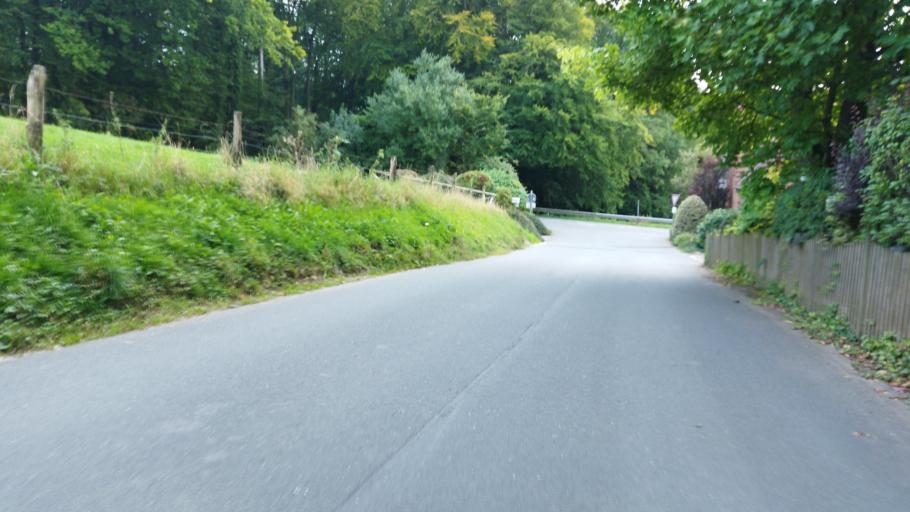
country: DE
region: Lower Saxony
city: Hagen
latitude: 52.1815
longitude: 8.0078
